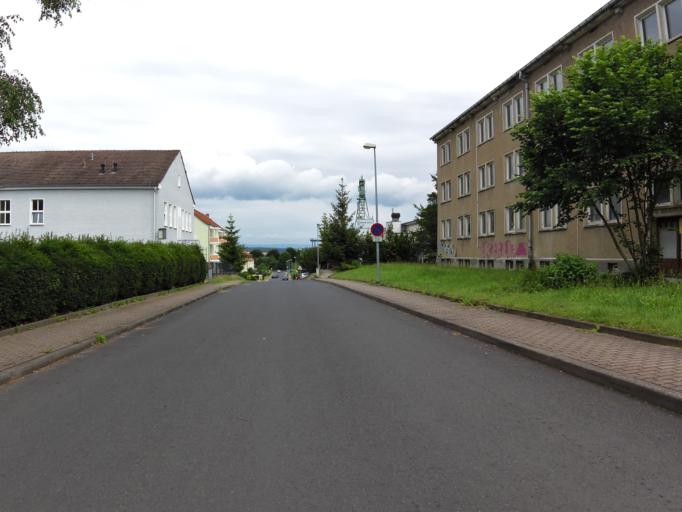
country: DE
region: Thuringia
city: Dorndorf
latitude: 50.8219
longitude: 10.1170
